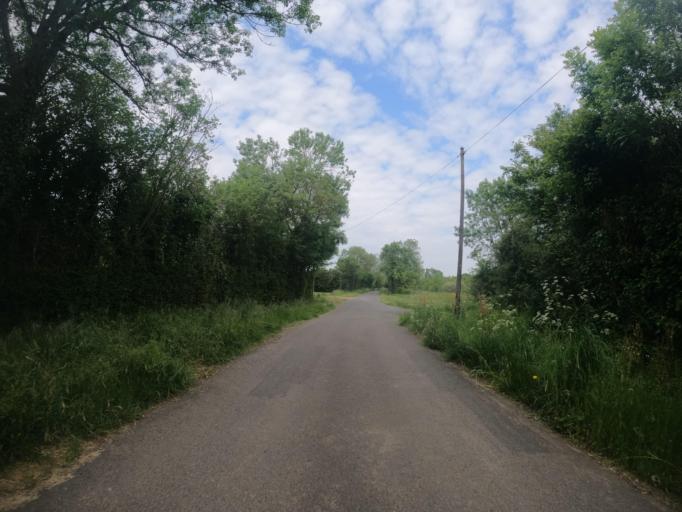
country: FR
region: Poitou-Charentes
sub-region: Departement des Deux-Sevres
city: Saint-Varent
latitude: 46.8777
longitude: -0.2814
